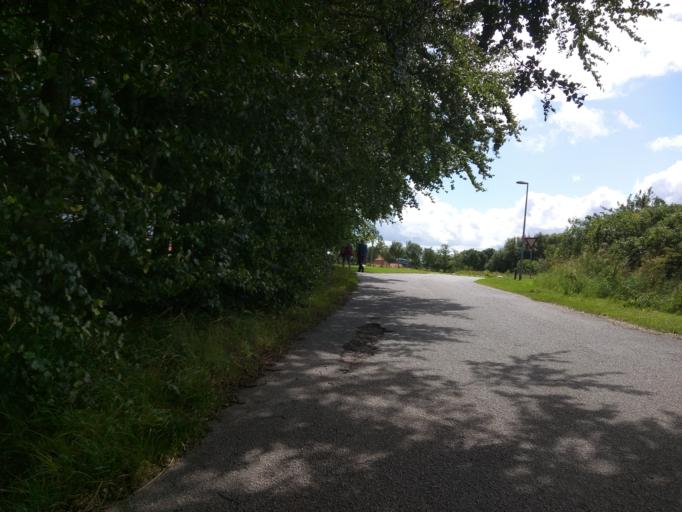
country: DK
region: Central Jutland
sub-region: Viborg Kommune
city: Viborg
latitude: 56.4320
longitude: 9.4059
